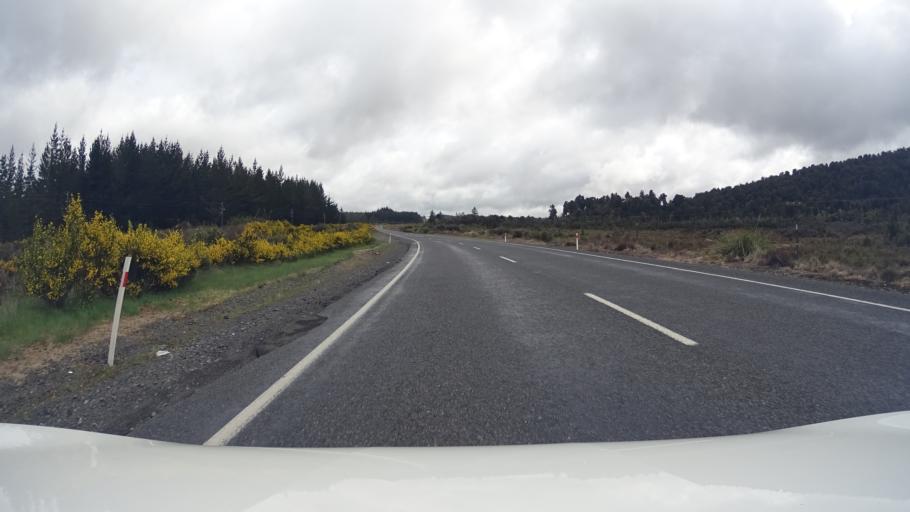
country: NZ
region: Manawatu-Wanganui
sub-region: Ruapehu District
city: Waiouru
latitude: -39.2209
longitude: 175.4007
